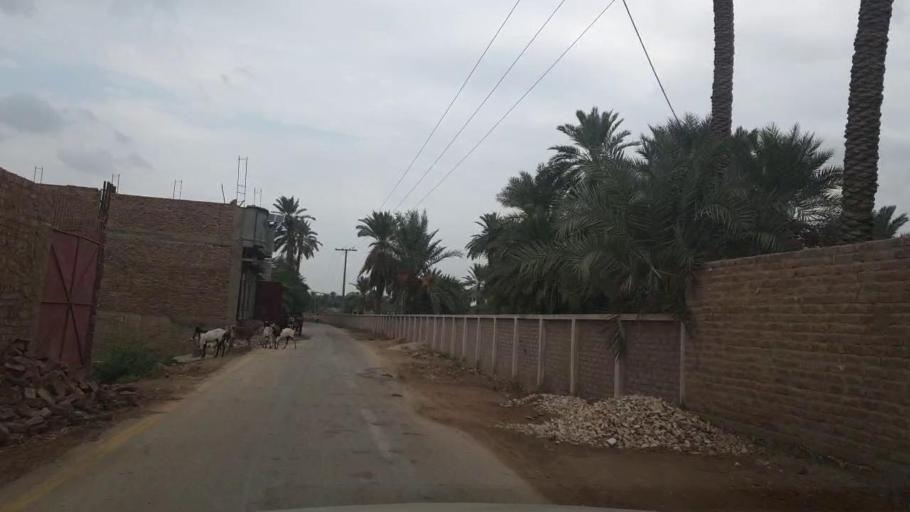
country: PK
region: Sindh
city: Khairpur
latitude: 27.5434
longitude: 68.7550
